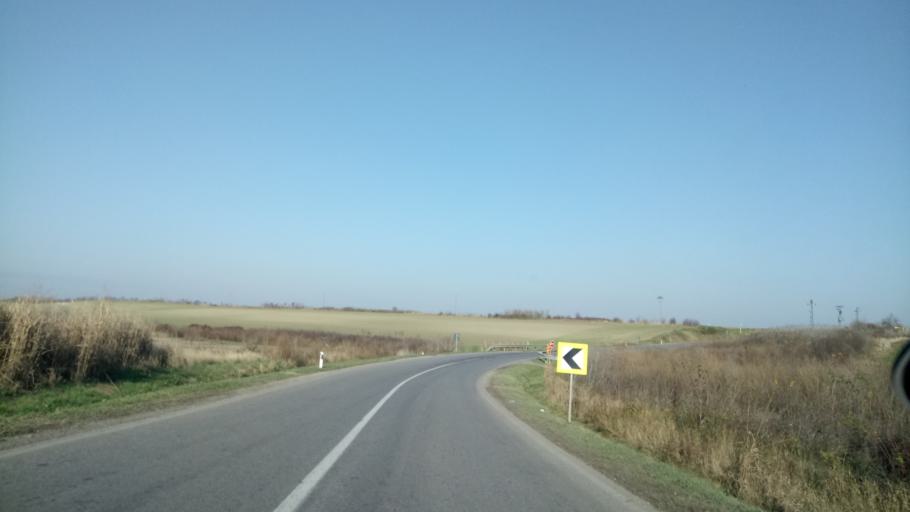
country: RS
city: Ljukovo
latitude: 45.0277
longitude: 20.0465
